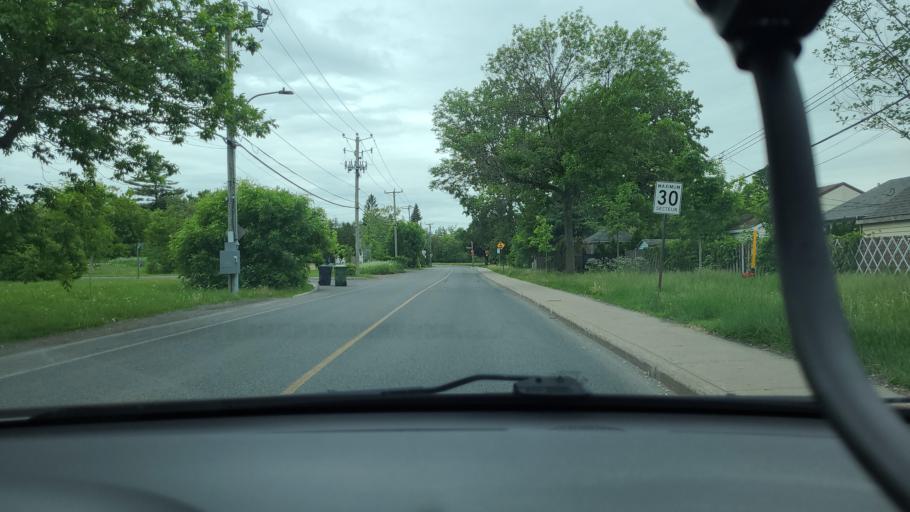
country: CA
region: Quebec
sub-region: Lanaudiere
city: Charlemagne
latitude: 45.6974
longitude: -73.4928
